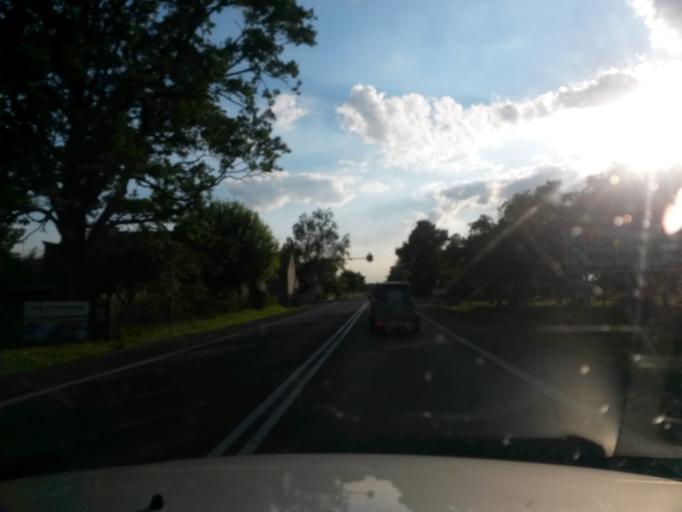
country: PL
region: Lodz Voivodeship
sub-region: Powiat belchatowski
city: Rusiec
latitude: 51.3129
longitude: 18.9079
